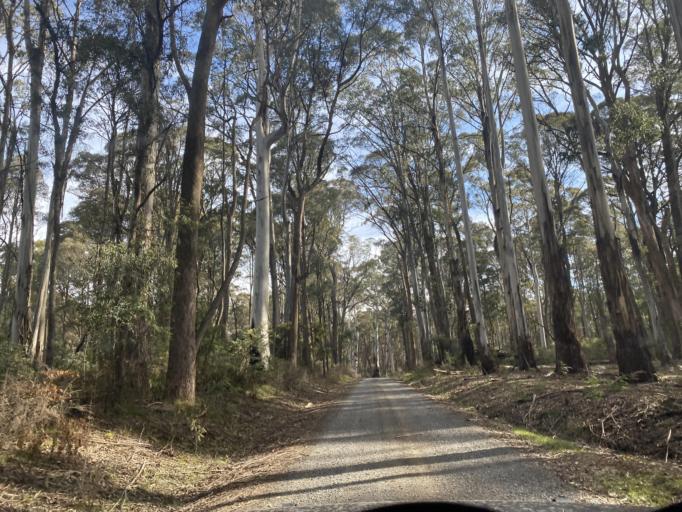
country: AU
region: Victoria
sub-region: Mansfield
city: Mansfield
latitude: -36.8680
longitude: 146.1993
